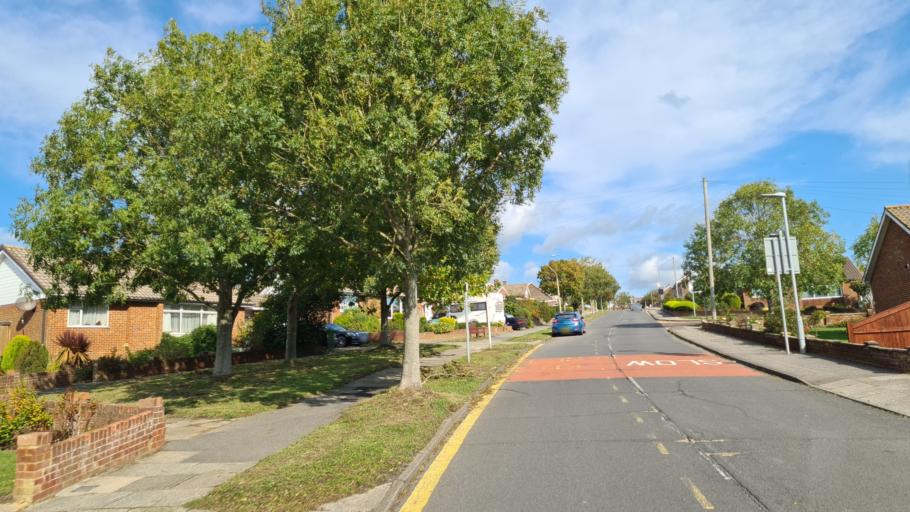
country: GB
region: England
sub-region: East Sussex
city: Hastings
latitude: 50.8775
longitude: 0.5677
